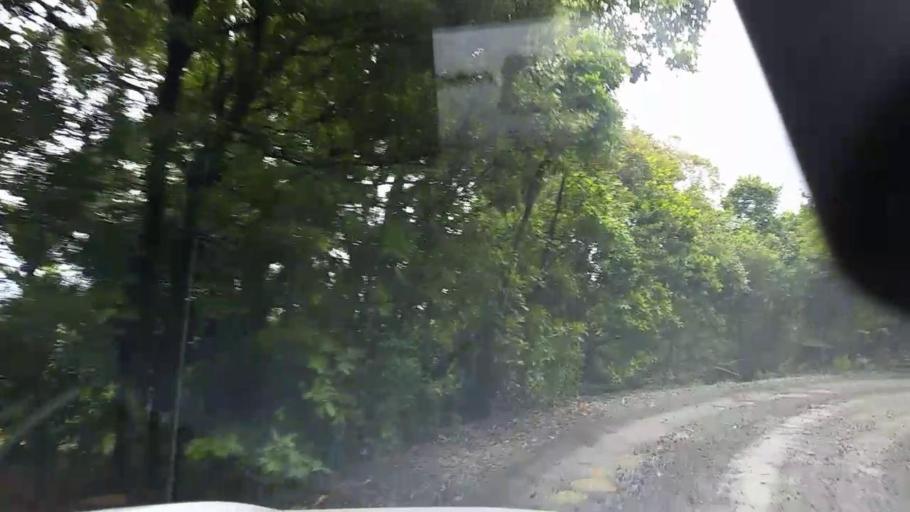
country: NZ
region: Auckland
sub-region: Auckland
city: Titirangi
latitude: -36.9417
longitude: 174.5193
